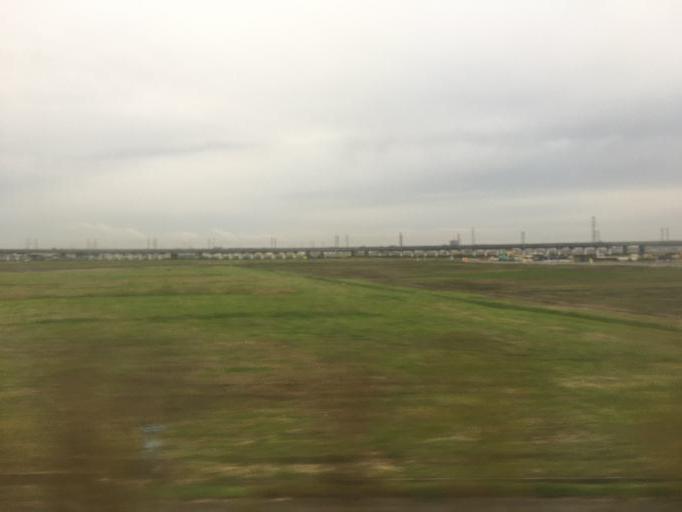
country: JP
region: Miyagi
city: Rifu
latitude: 38.2950
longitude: 140.9437
